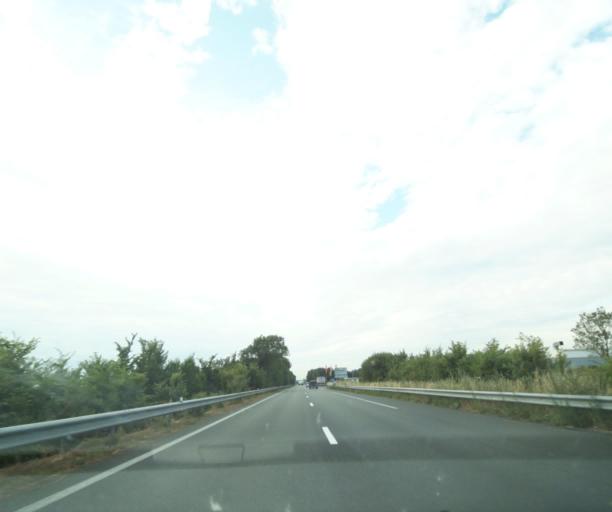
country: FR
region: Poitou-Charentes
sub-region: Departement de la Charente-Maritime
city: Chatelaillon-Plage
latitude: 46.0764
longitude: -1.0731
